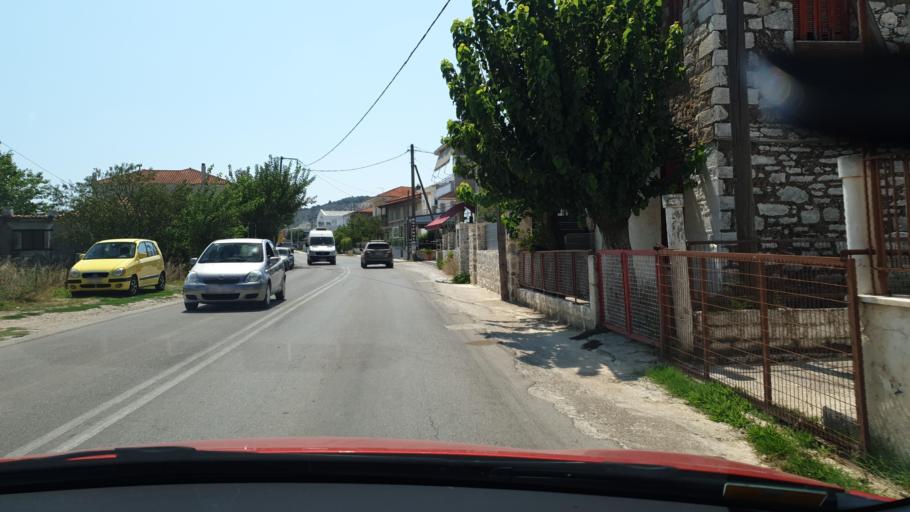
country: GR
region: Central Greece
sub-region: Nomos Evvoias
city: Aliveri
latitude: 38.4517
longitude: 24.1134
